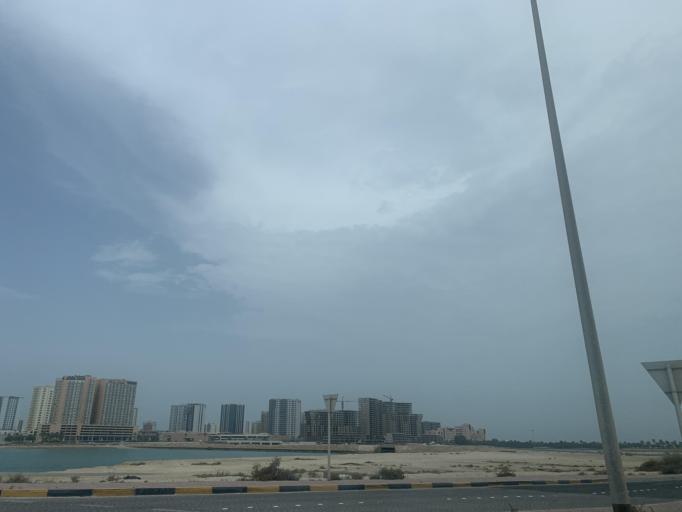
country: BH
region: Muharraq
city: Al Hadd
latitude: 26.2833
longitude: 50.6552
